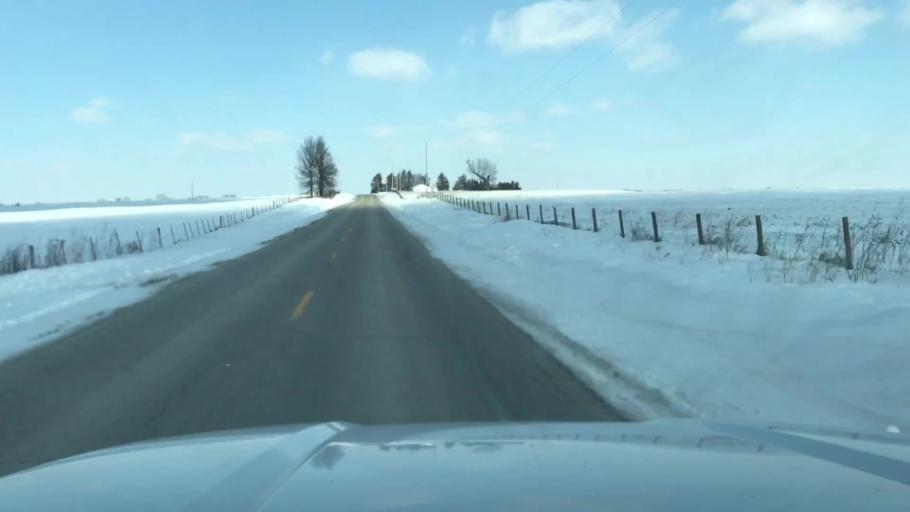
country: US
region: Missouri
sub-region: Nodaway County
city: Maryville
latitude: 40.3695
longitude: -94.7216
